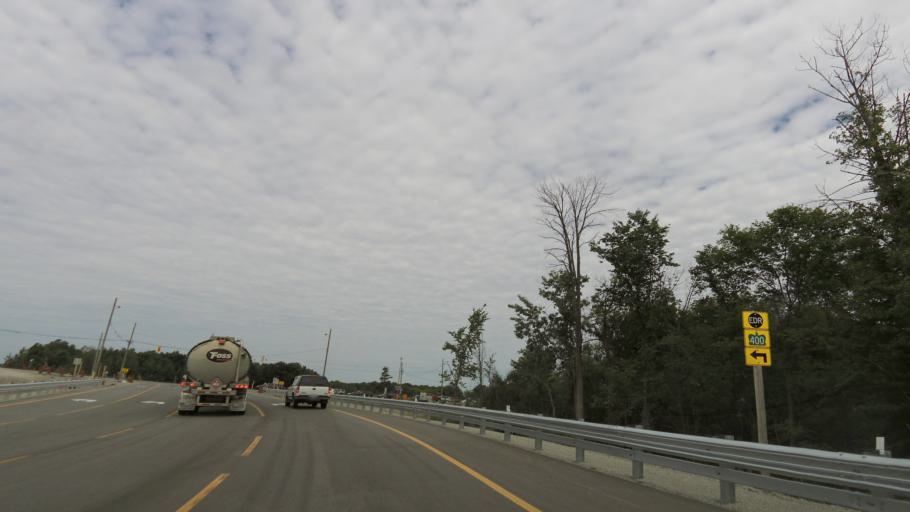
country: CA
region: Ontario
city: Bradford West Gwillimbury
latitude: 44.0289
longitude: -79.5921
